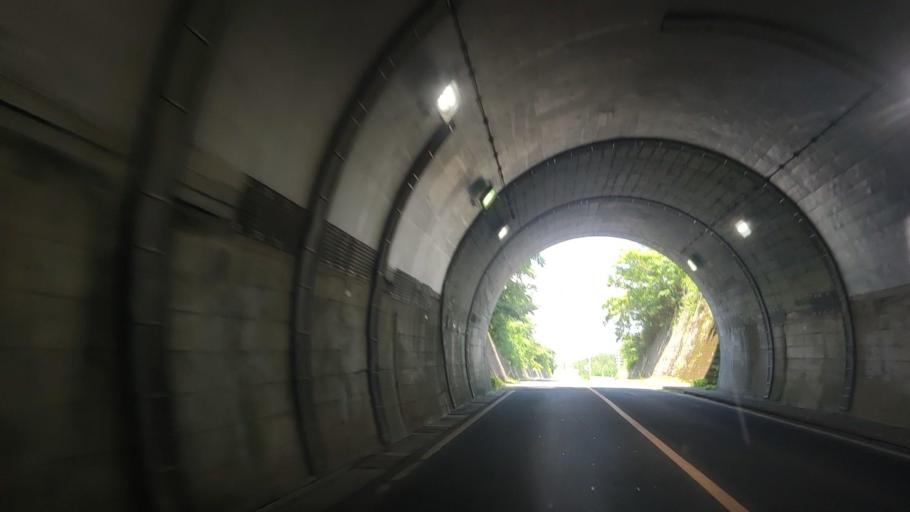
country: JP
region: Tottori
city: Tottori
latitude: 35.5321
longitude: 134.2301
